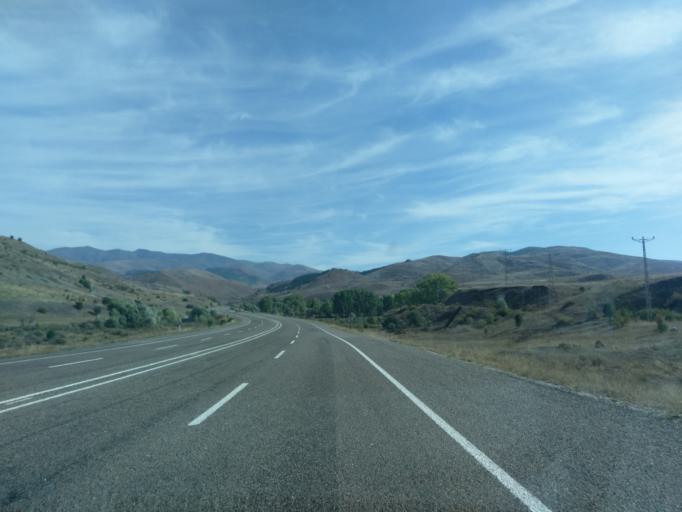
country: TR
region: Sivas
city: Imranli
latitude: 39.8389
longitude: 38.2815
